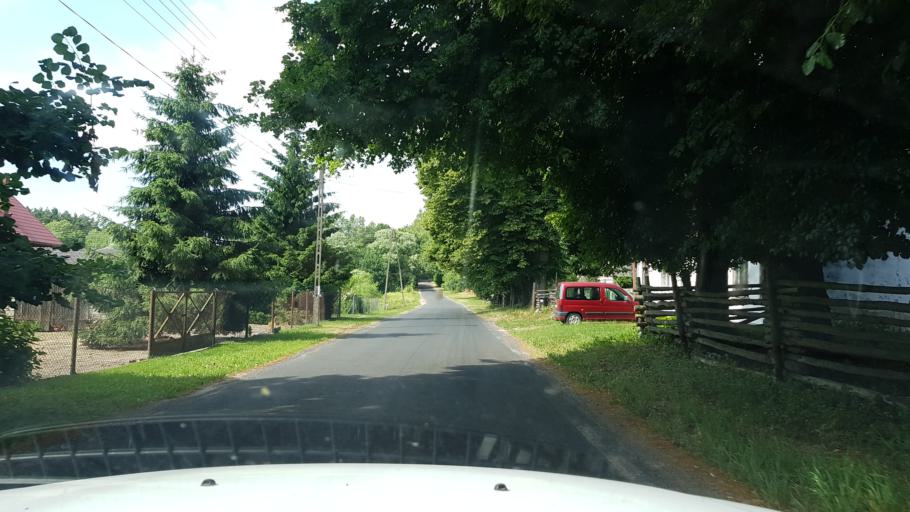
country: PL
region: West Pomeranian Voivodeship
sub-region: Powiat goleniowski
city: Mosty
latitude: 53.5645
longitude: 14.9748
